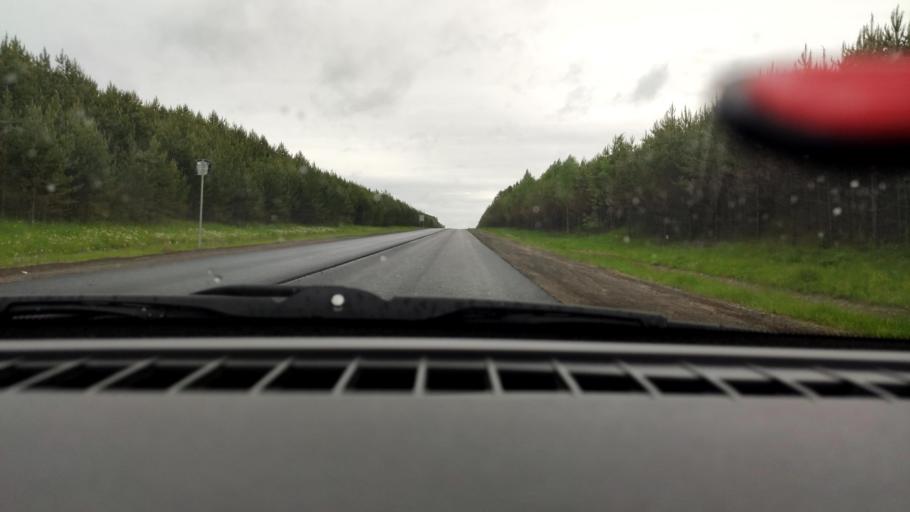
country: RU
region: Perm
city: Karagay
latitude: 58.2564
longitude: 54.8933
